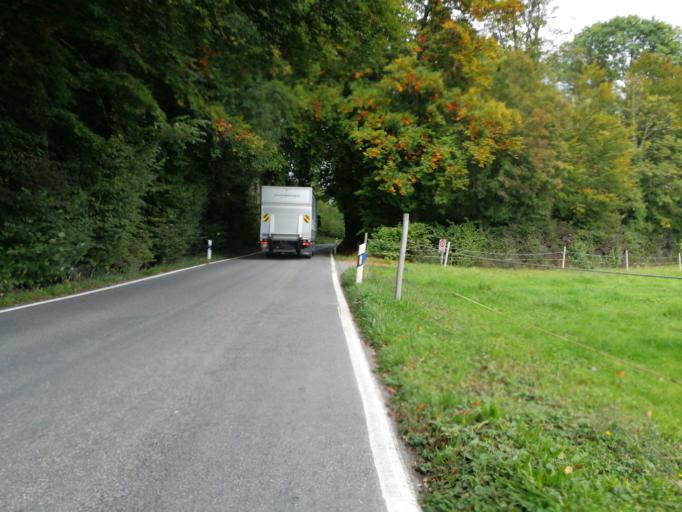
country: CH
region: Zurich
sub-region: Bezirk Meilen
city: Dorf
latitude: 47.2525
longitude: 8.7400
